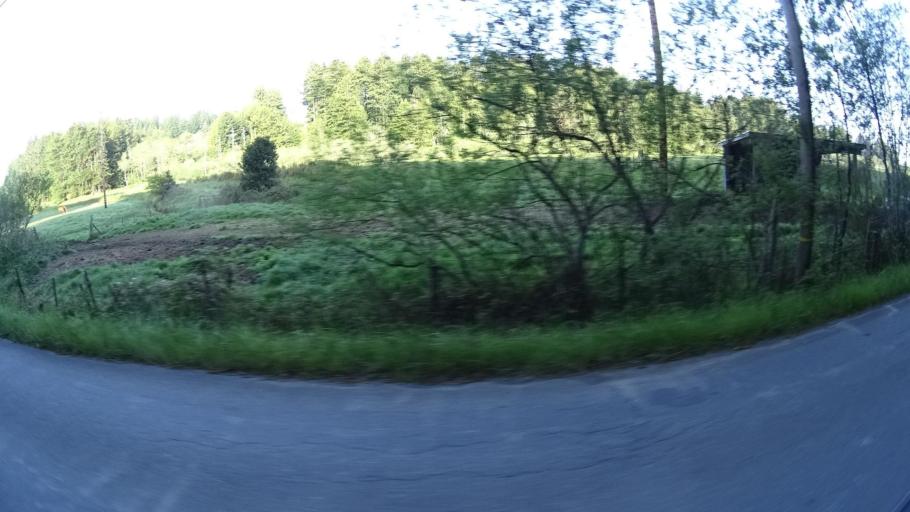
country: US
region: California
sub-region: Humboldt County
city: Myrtletown
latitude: 40.7809
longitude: -124.1181
